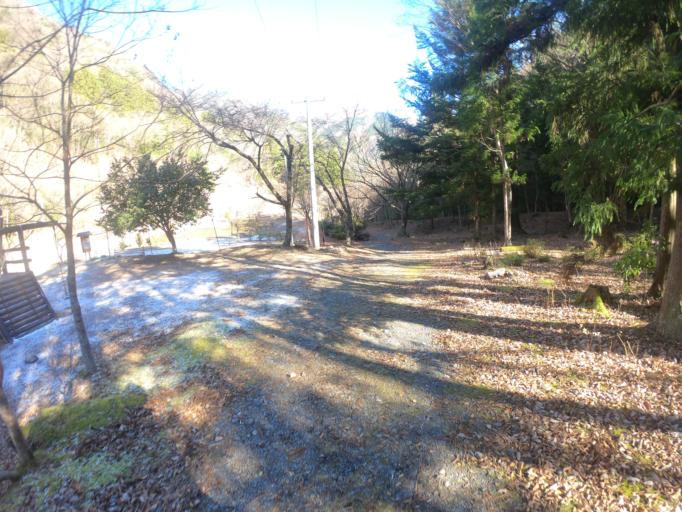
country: JP
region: Shizuoka
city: Shizuoka-shi
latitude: 35.1766
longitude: 138.1186
